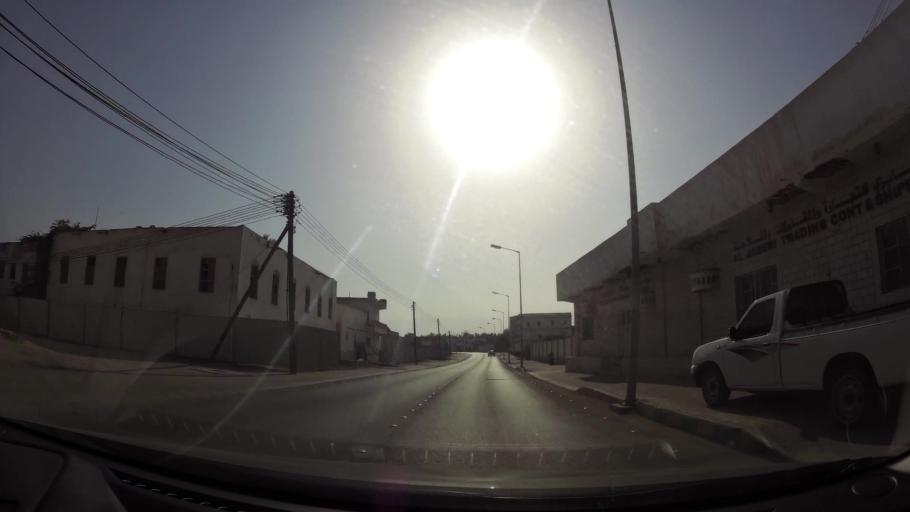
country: OM
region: Zufar
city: Salalah
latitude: 17.0032
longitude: 54.1093
